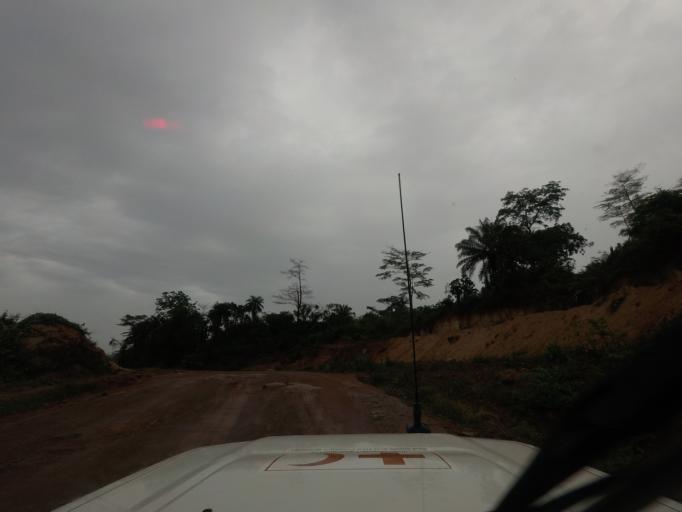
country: LR
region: Nimba
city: Sanniquellie
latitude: 7.2602
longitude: -8.8487
